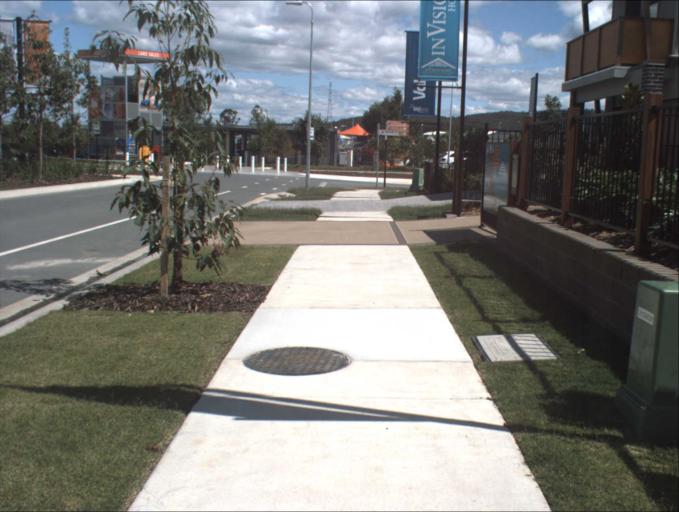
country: AU
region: Queensland
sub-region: Logan
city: Chambers Flat
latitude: -27.8055
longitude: 153.1161
